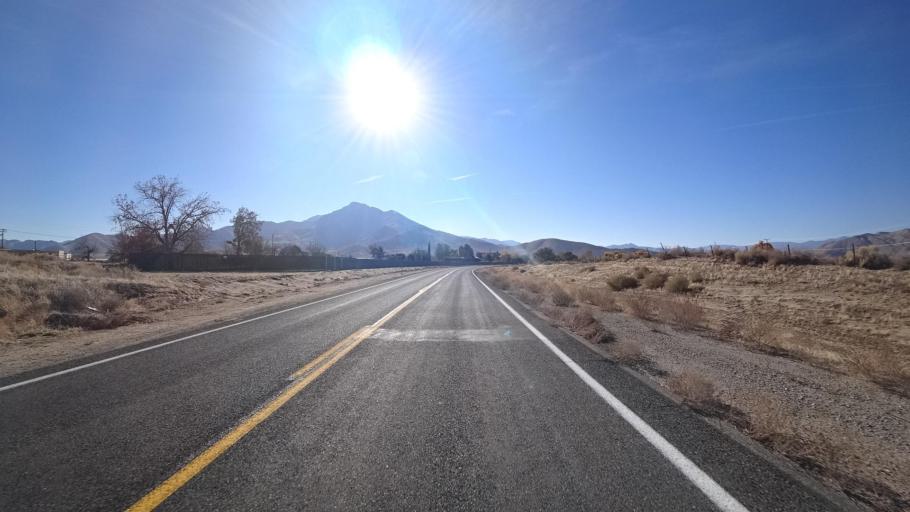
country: US
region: California
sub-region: Kern County
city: Weldon
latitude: 35.6692
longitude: -118.2639
